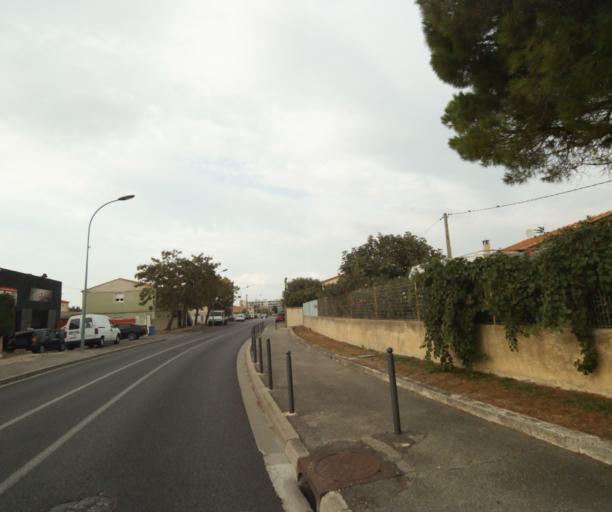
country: FR
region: Provence-Alpes-Cote d'Azur
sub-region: Departement des Bouches-du-Rhone
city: Marignane
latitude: 43.4050
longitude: 5.2157
